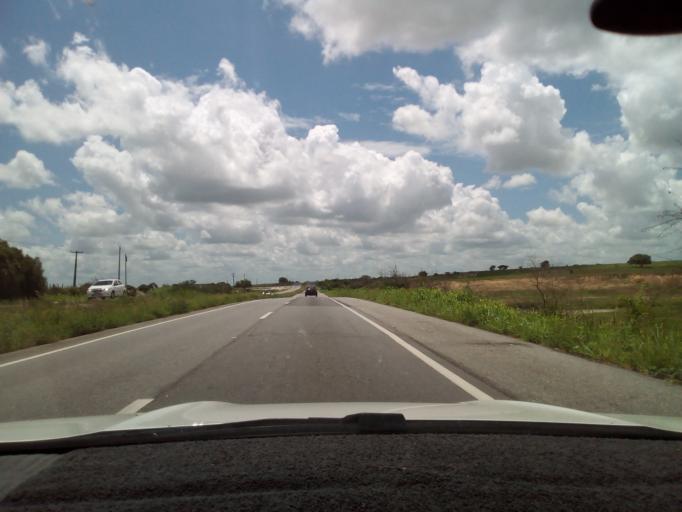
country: BR
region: Paraiba
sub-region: Gurinhem
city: Gurinhem
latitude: -7.1683
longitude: -35.3698
